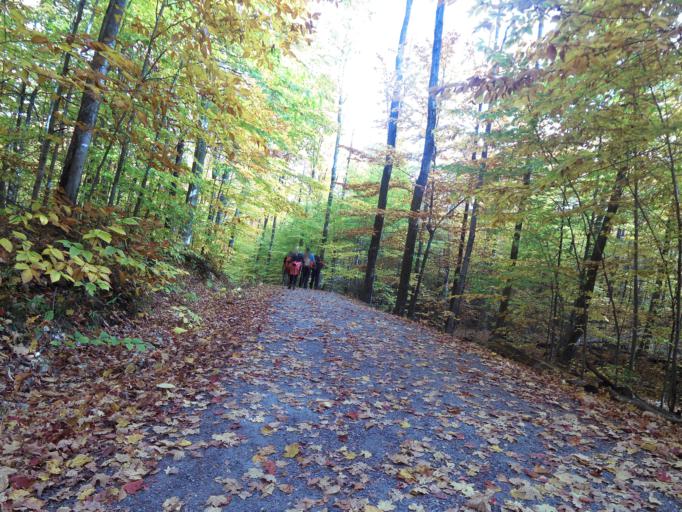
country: CA
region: Quebec
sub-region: Outaouais
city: Gatineau
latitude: 45.4984
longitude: -75.8349
